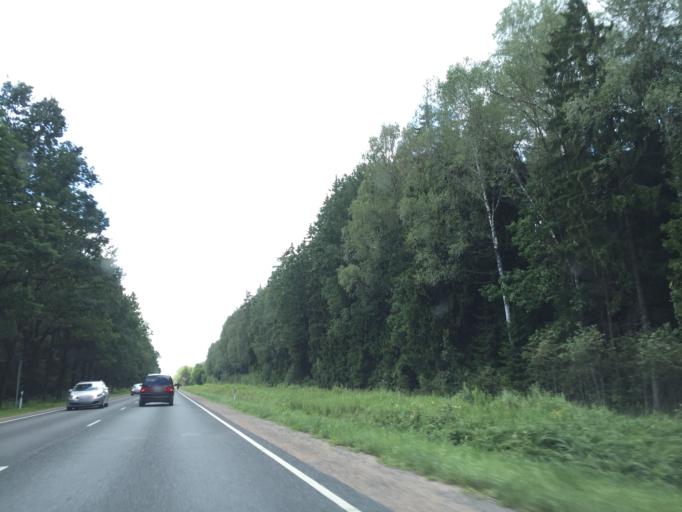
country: LV
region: Ozolnieku
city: Ozolnieki
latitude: 56.6985
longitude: 23.8081
